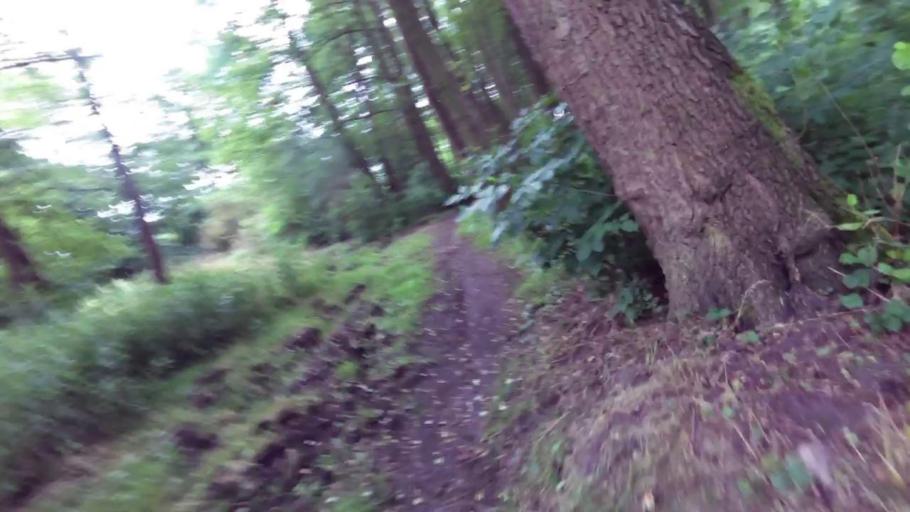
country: PL
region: West Pomeranian Voivodeship
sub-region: Powiat stargardzki
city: Chociwel
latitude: 53.4671
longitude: 15.3598
